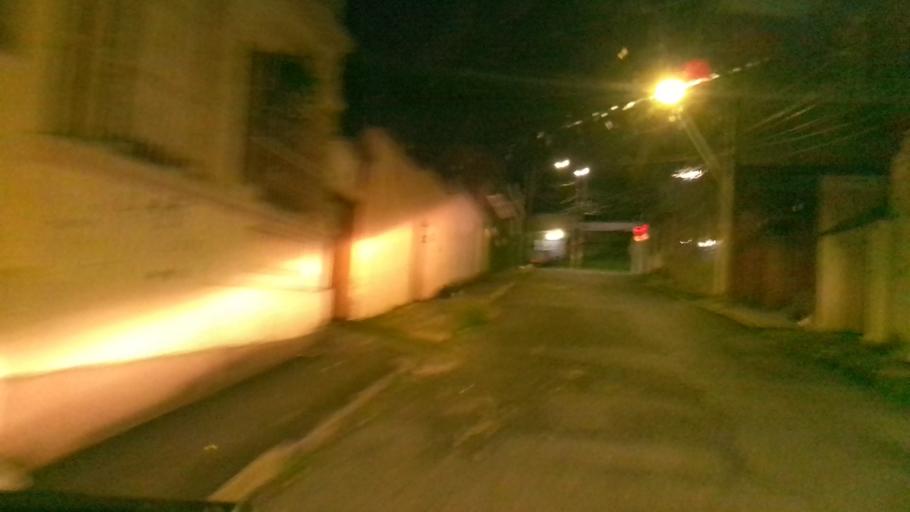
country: BR
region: Minas Gerais
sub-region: Belo Horizonte
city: Belo Horizonte
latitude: -19.9142
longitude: -43.9189
